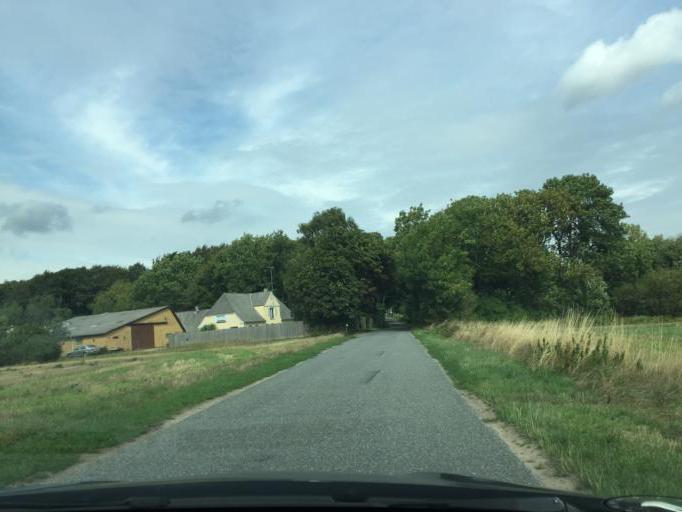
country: DK
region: South Denmark
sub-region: Assens Kommune
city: Vissenbjerg
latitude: 55.3602
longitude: 10.1429
